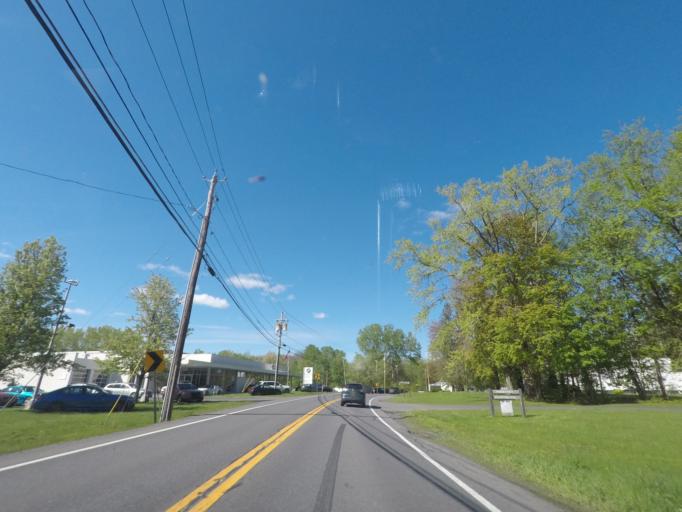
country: US
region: New York
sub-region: Albany County
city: Delmar
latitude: 42.5885
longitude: -73.7970
